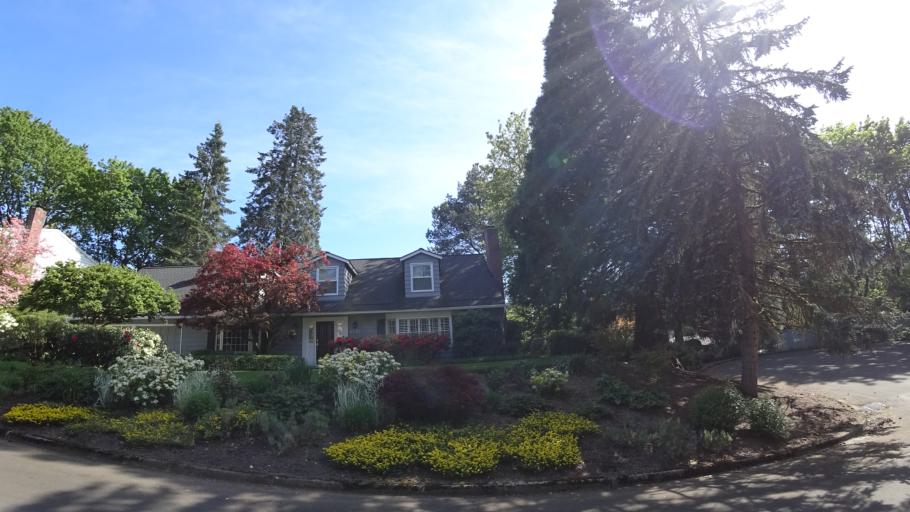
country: US
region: Oregon
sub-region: Washington County
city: West Slope
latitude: 45.4936
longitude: -122.7468
